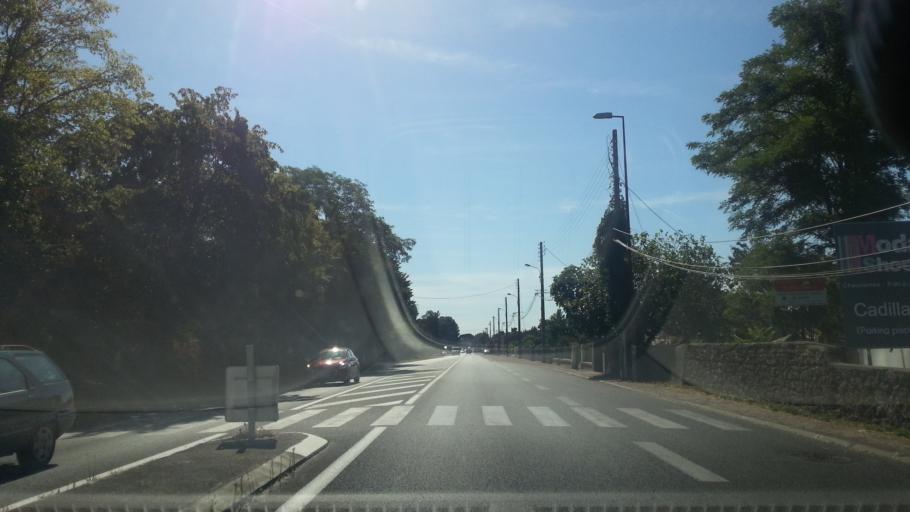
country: FR
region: Aquitaine
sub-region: Departement de la Gironde
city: Podensac
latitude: 44.6556
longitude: -0.3643
